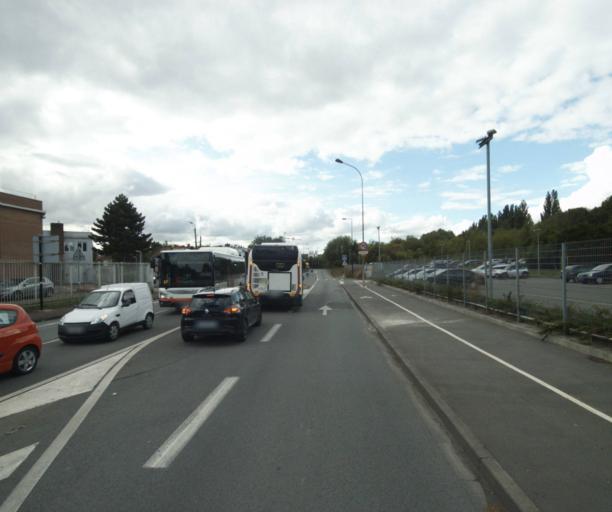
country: FR
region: Nord-Pas-de-Calais
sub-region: Departement du Nord
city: Sequedin
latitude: 50.6331
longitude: 2.9903
